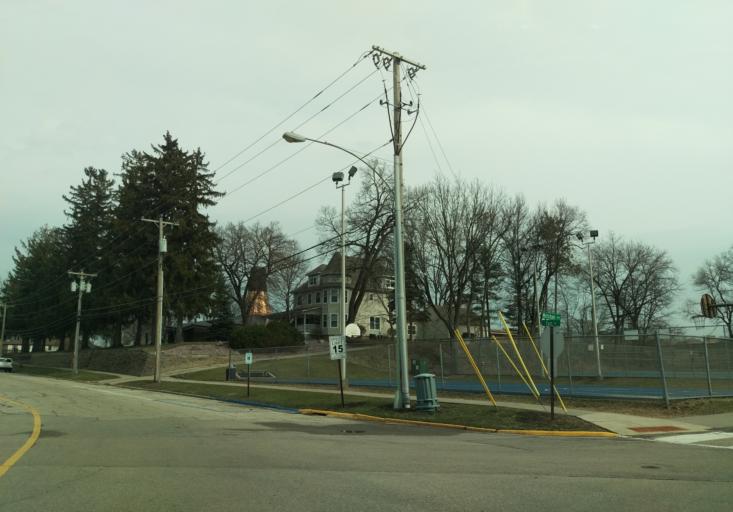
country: US
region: Wisconsin
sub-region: Columbia County
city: Lodi
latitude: 43.3171
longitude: -89.5277
